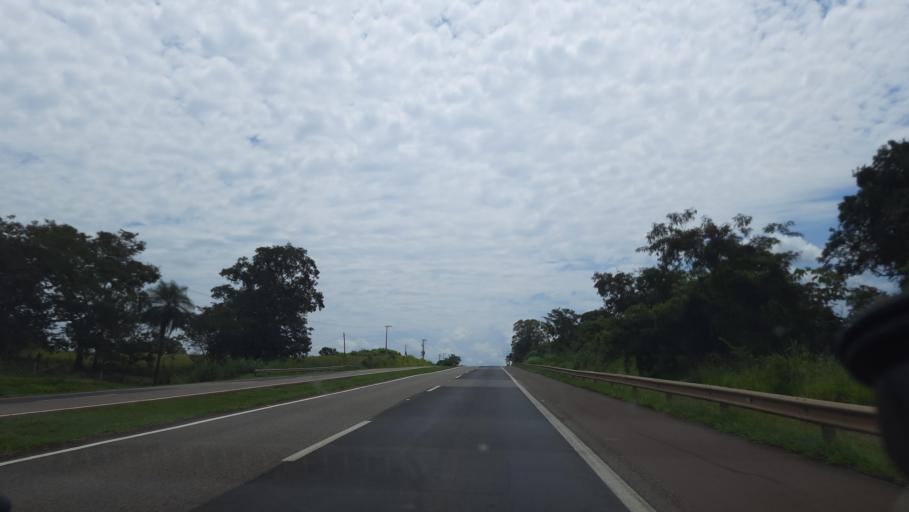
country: BR
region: Sao Paulo
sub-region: Casa Branca
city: Casa Branca
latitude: -21.7262
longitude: -47.0775
